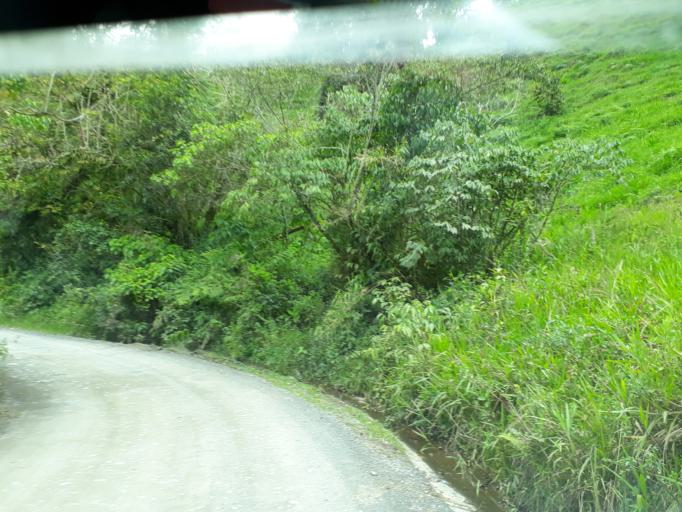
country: CO
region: Cundinamarca
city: Pacho
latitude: 5.2563
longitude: -74.1897
